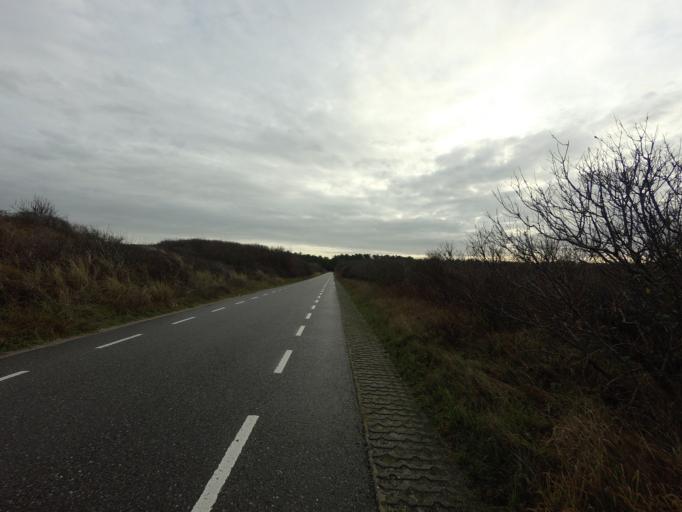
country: NL
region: North Holland
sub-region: Gemeente Texel
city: Den Burg
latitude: 53.0563
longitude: 4.7308
